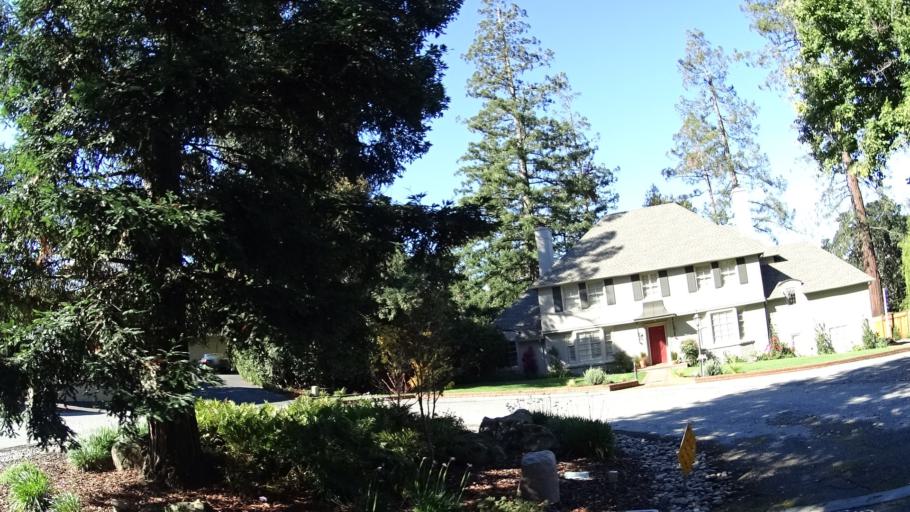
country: US
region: California
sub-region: San Mateo County
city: Burlingame
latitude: 37.5756
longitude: -122.3616
